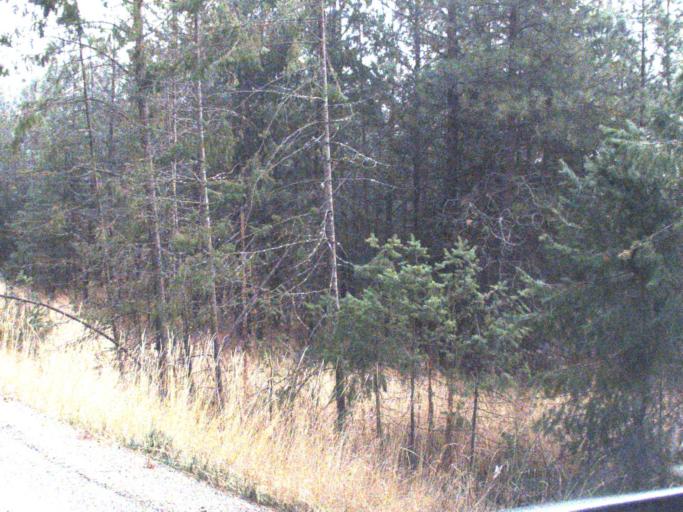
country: CA
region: British Columbia
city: Grand Forks
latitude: 48.8995
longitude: -118.2139
